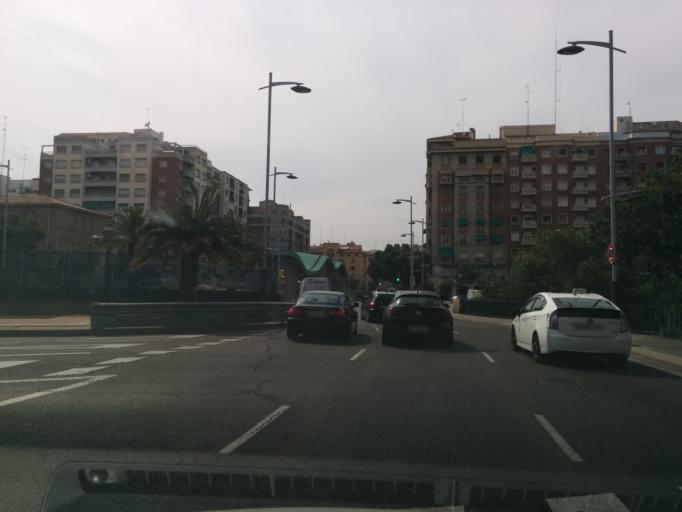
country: ES
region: Aragon
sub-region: Provincia de Zaragoza
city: Zaragoza
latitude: 41.6435
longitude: -0.8898
